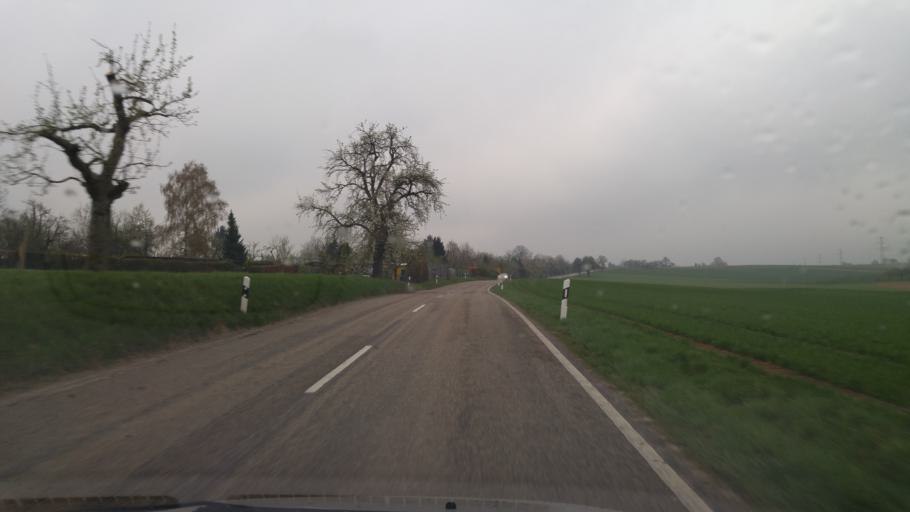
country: DE
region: Baden-Wuerttemberg
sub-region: Regierungsbezirk Stuttgart
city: Leonberg
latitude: 48.8313
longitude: 9.0272
